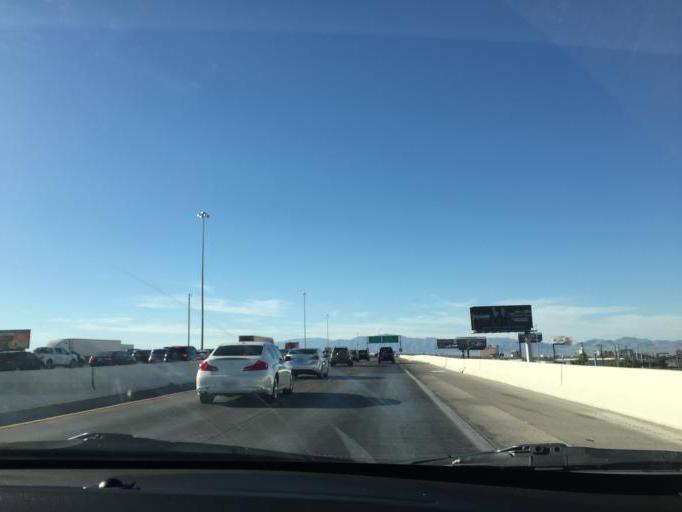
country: US
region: Nevada
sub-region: Clark County
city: Paradise
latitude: 36.1200
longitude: -115.1802
